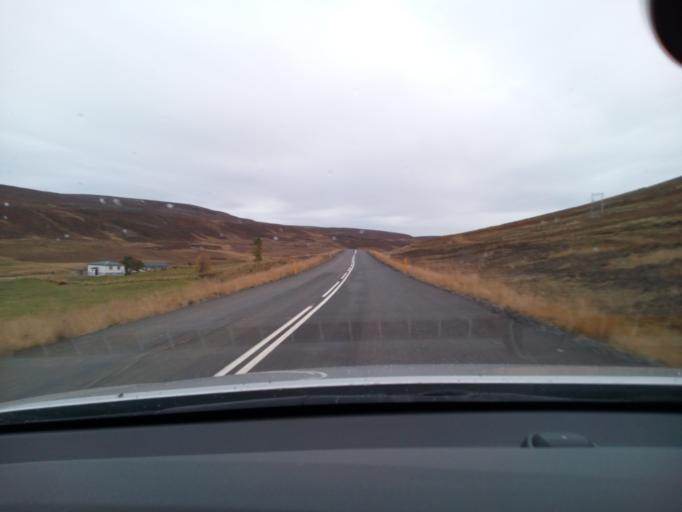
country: IS
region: Northeast
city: Laugar
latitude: 65.7989
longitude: -17.2529
